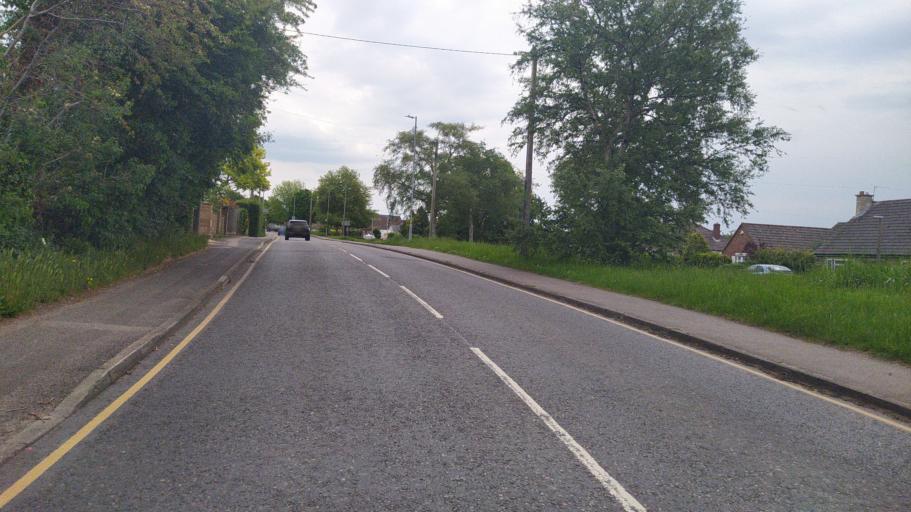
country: GB
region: England
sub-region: Wiltshire
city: Melksham
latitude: 51.3765
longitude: -2.1312
